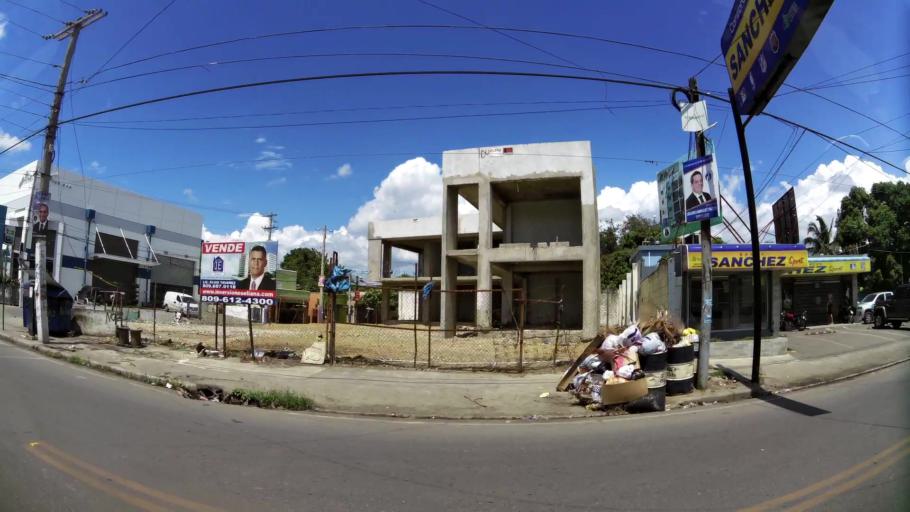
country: DO
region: Santiago
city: Santiago de los Caballeros
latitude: 19.4748
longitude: -70.6763
